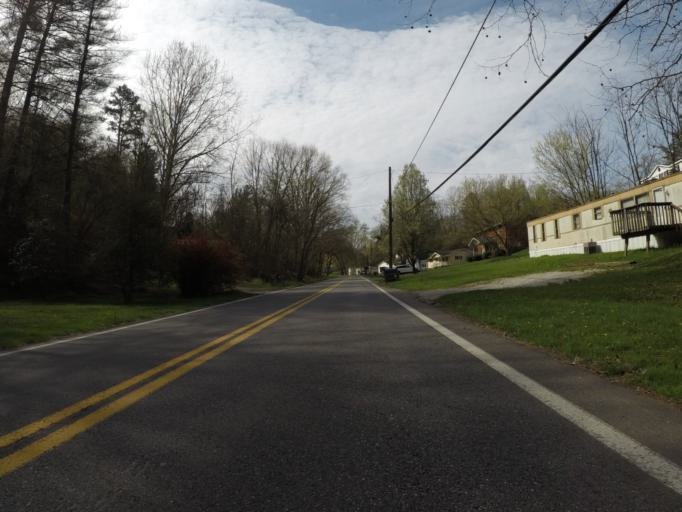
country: US
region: West Virginia
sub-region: Cabell County
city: Pea Ridge
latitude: 38.3735
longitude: -82.3705
